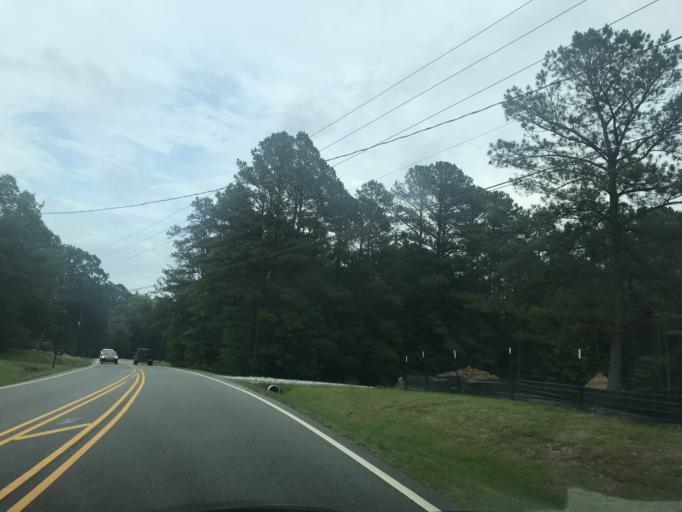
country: US
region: North Carolina
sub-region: Wake County
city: Green Level
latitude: 35.8235
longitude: -78.8833
